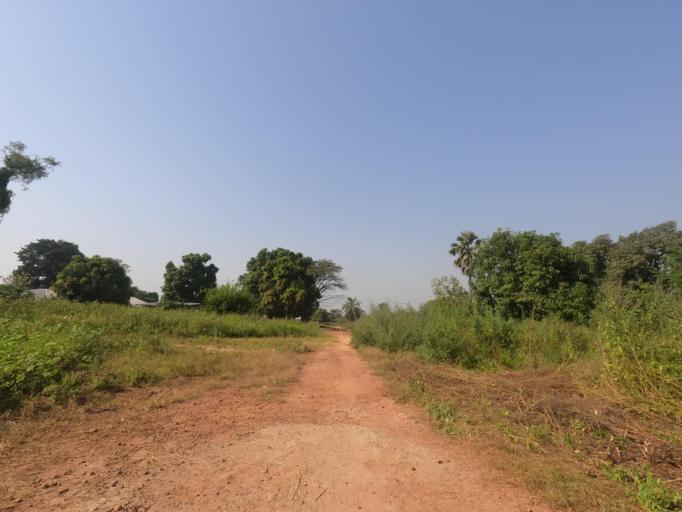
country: SN
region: Sedhiou
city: Sedhiou
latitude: 12.4447
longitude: -15.7391
